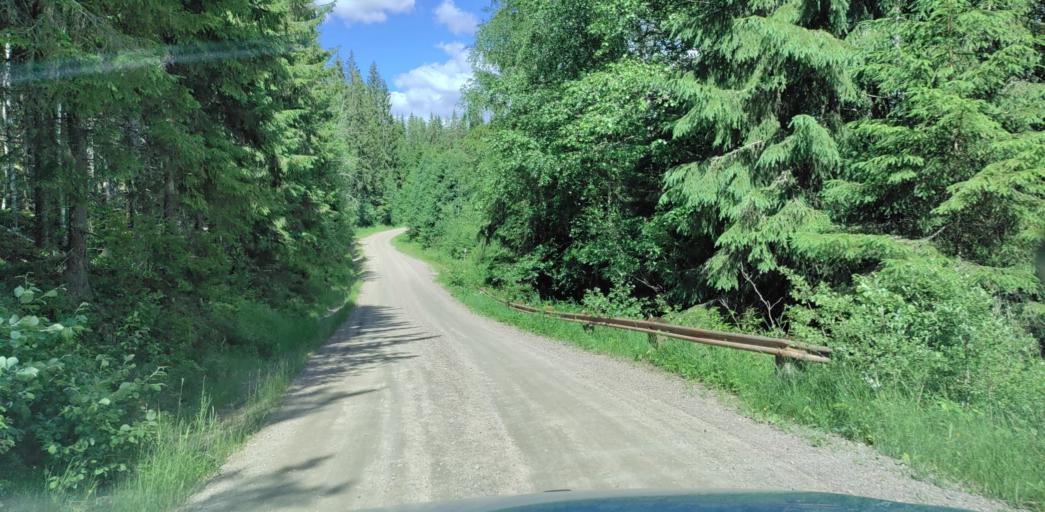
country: SE
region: Vaermland
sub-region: Sunne Kommun
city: Sunne
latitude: 60.0479
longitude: 13.2581
